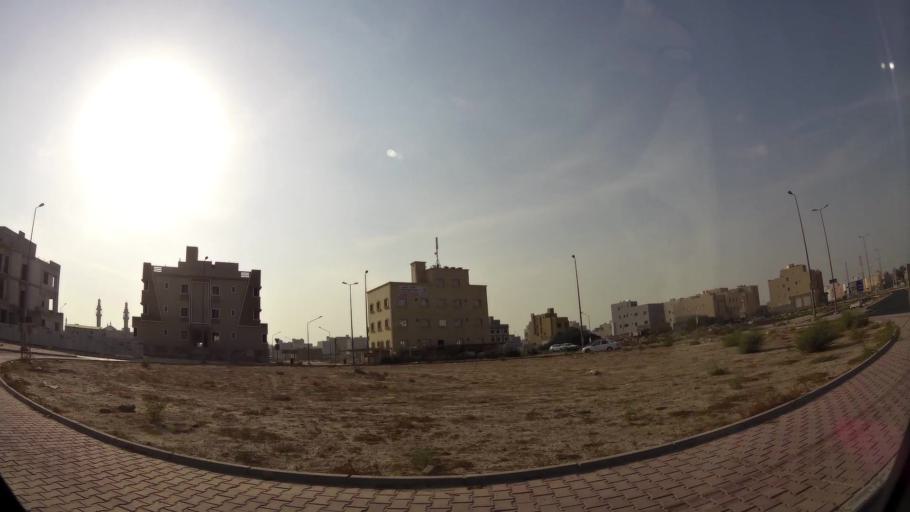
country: KW
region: Mubarak al Kabir
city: Mubarak al Kabir
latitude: 29.1917
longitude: 48.1061
